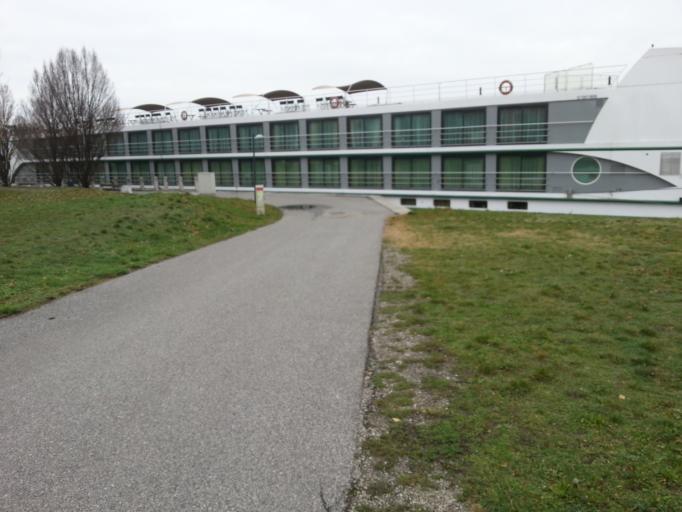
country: AT
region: Vienna
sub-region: Wien Stadt
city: Vienna
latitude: 48.2125
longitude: 16.4239
